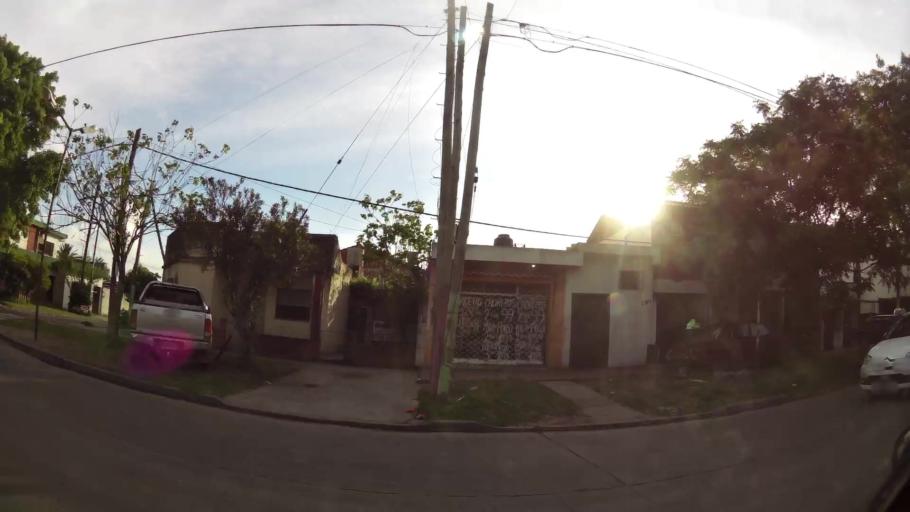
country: AR
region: Buenos Aires
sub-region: Partido de Quilmes
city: Quilmes
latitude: -34.7428
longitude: -58.2676
